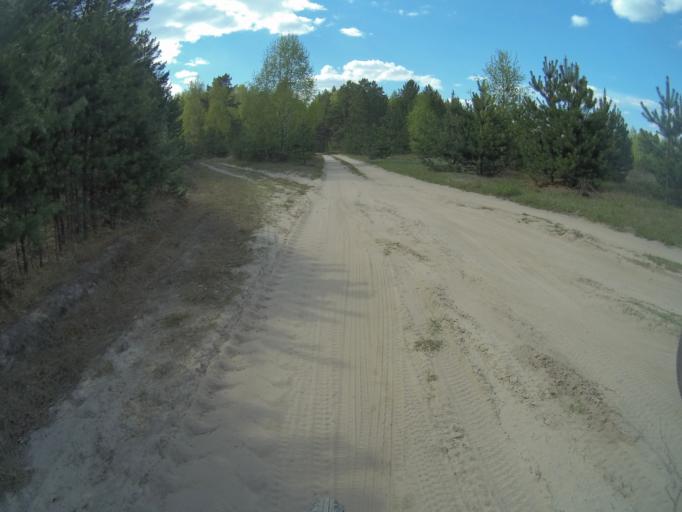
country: RU
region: Vladimir
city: Vorsha
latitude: 55.9669
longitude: 40.1789
